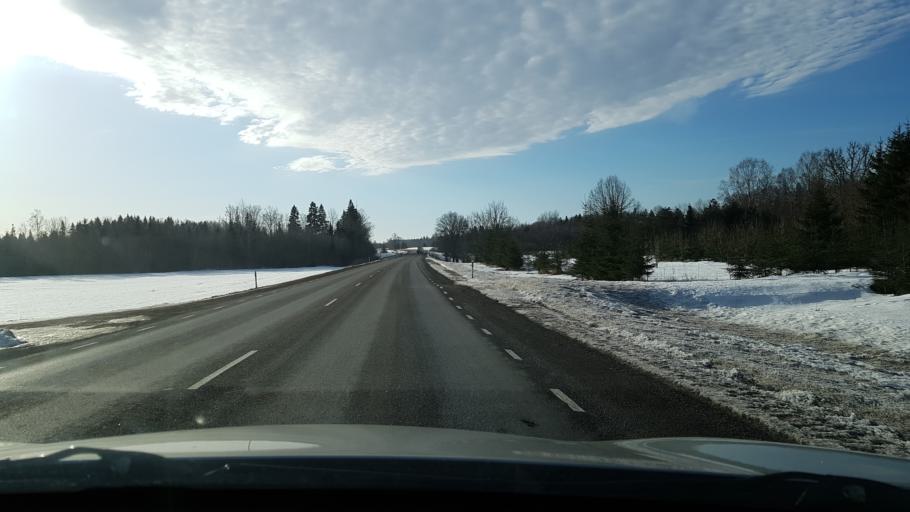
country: EE
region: Viljandimaa
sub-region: Viljandi linn
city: Viljandi
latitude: 58.4399
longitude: 25.5952
